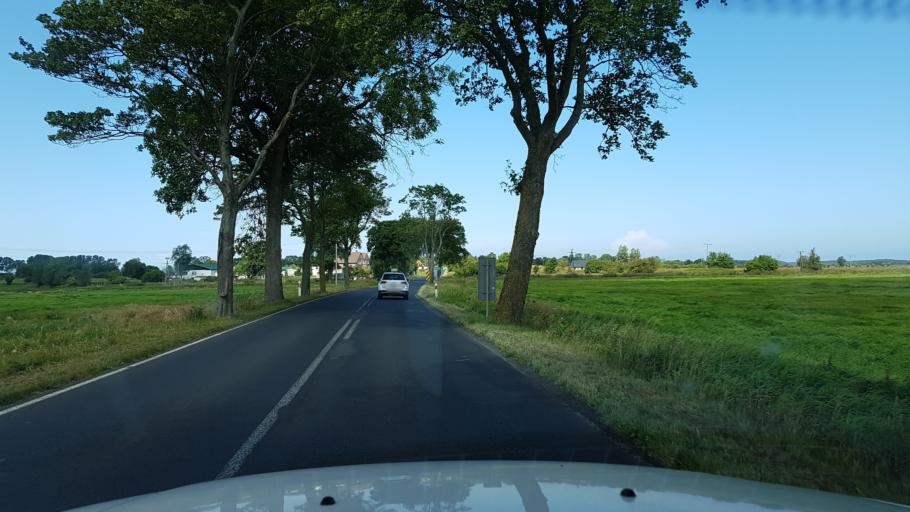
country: PL
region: West Pomeranian Voivodeship
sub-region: Powiat gryficki
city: Trzebiatow
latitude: 54.0750
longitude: 15.2240
